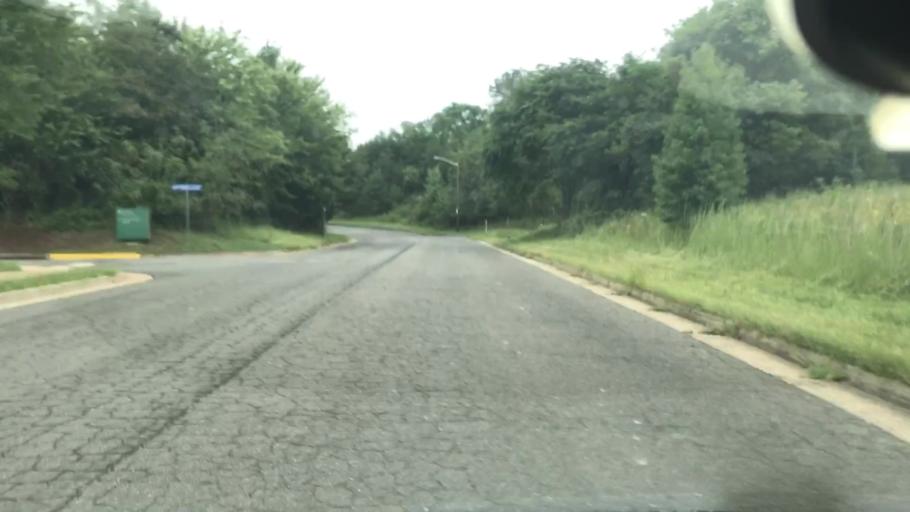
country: US
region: Virginia
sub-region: Fairfax County
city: Newington
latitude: 38.7640
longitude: -77.1786
